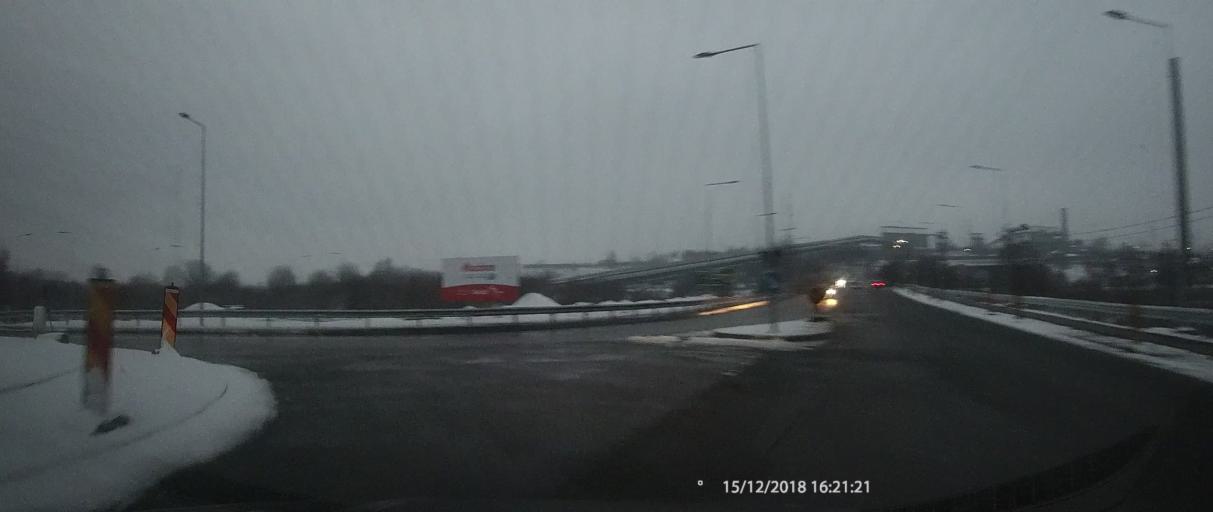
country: RO
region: Galati
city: Galati
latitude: 45.4086
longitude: 27.9992
